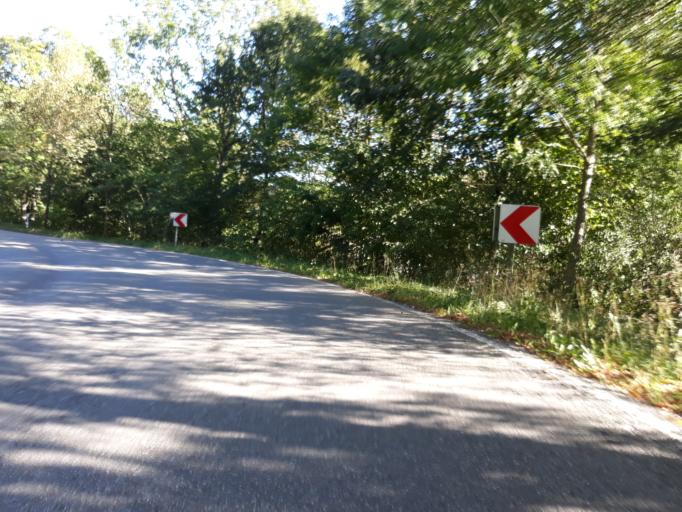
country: DE
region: Baden-Wuerttemberg
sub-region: Regierungsbezirk Stuttgart
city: Ehningen
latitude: 48.6641
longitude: 8.9178
